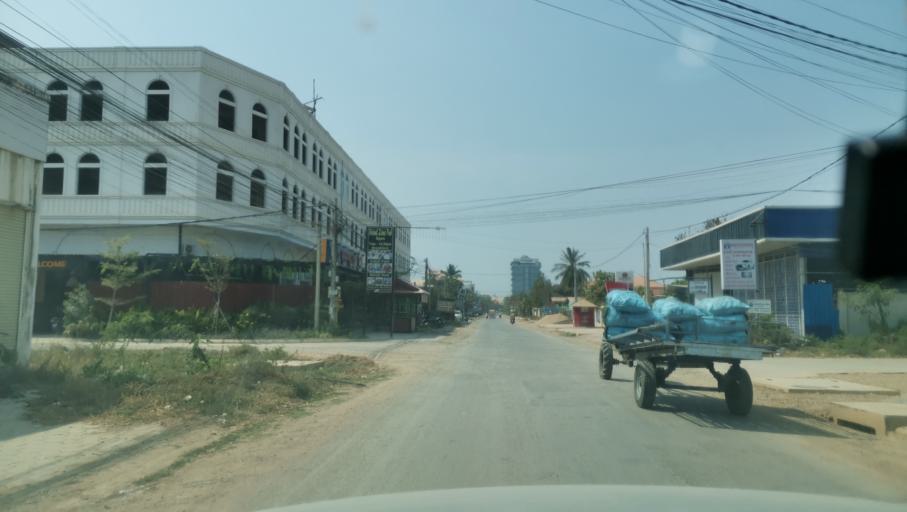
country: KH
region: Battambang
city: Battambang
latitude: 13.0986
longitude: 103.2042
